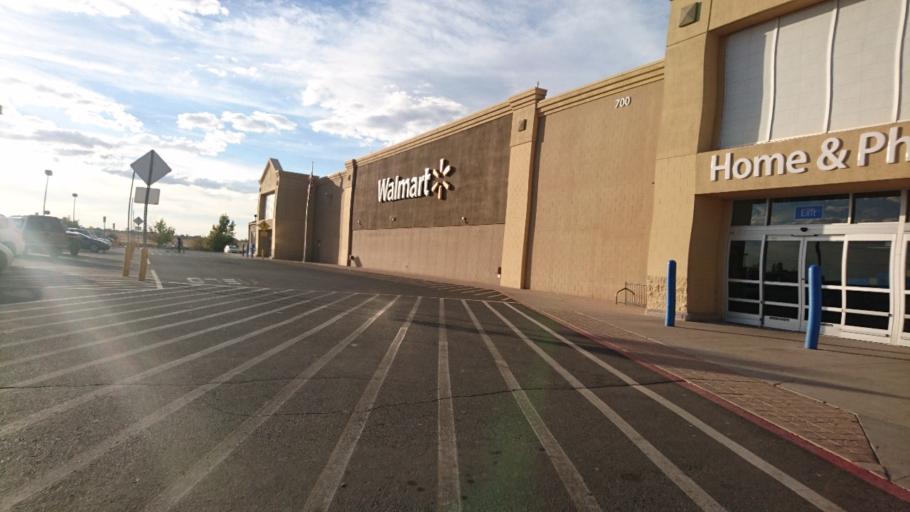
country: US
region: Arizona
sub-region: Navajo County
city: Winslow
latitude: 35.0426
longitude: -110.7012
